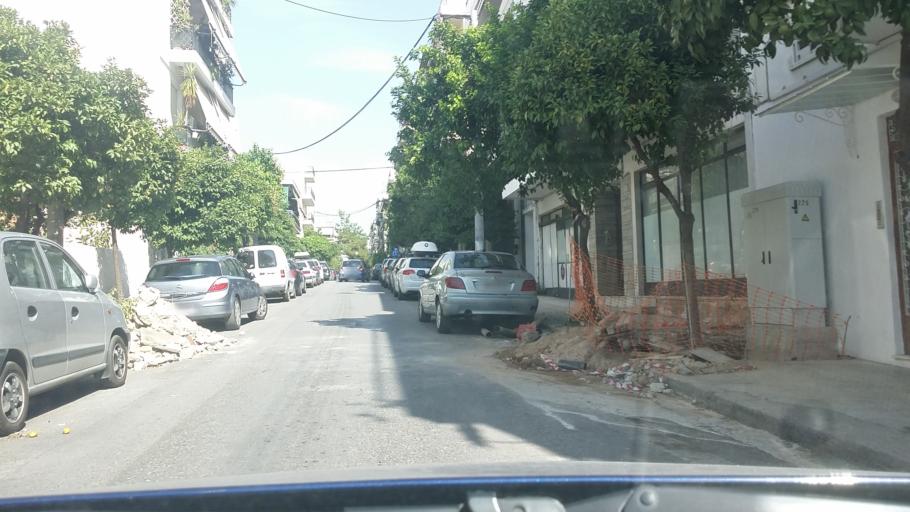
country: GR
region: Attica
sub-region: Nomarchia Athinas
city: Nea Ionia
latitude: 38.0356
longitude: 23.7698
